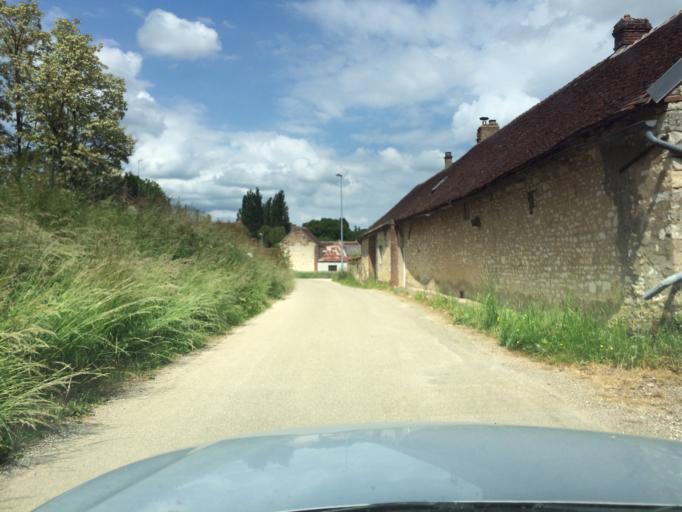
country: FR
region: Bourgogne
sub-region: Departement de l'Yonne
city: Fleury-la-Vallee
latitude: 47.8920
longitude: 3.4274
